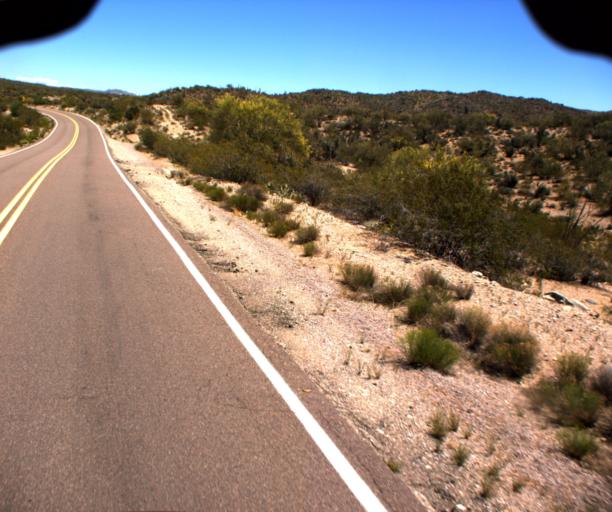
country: US
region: Arizona
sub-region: Yavapai County
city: Bagdad
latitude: 34.4735
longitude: -113.2108
